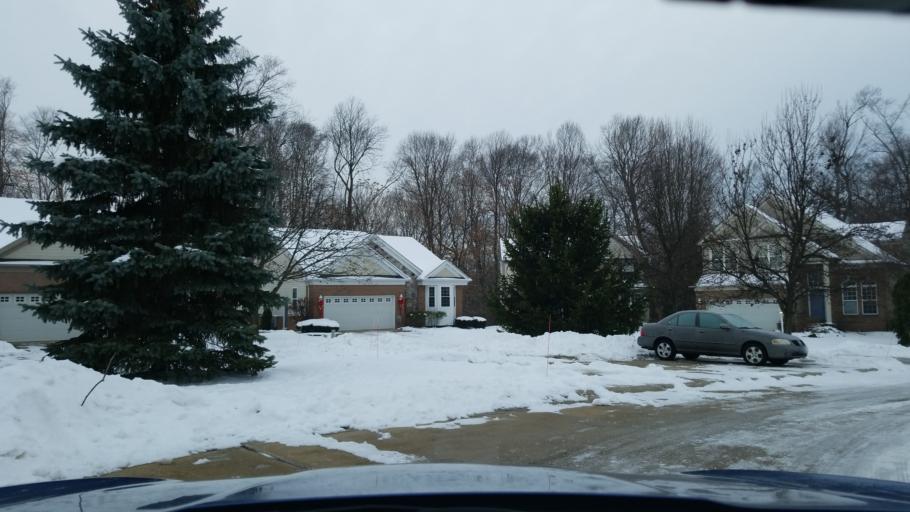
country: US
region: Ohio
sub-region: Summit County
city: Northfield
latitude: 41.3316
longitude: -81.5375
